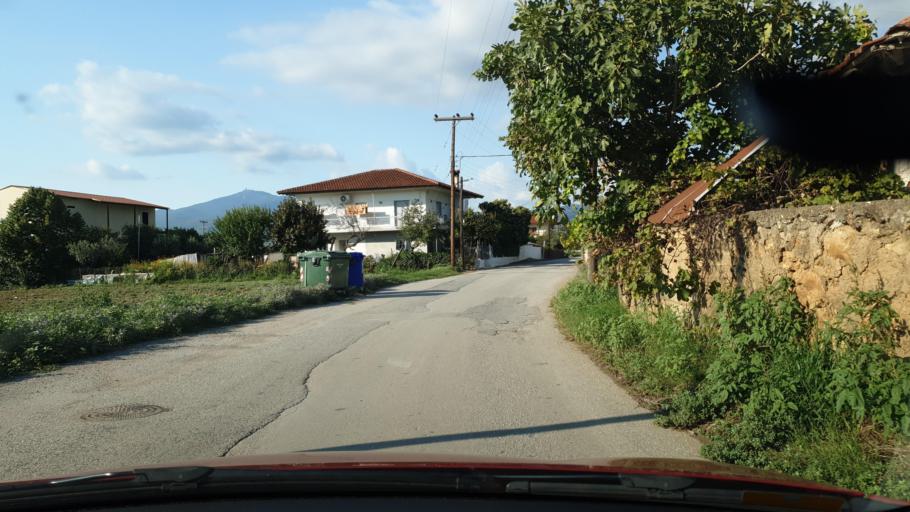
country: GR
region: Central Macedonia
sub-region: Nomos Thessalonikis
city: Vasilika
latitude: 40.4877
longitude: 23.1381
